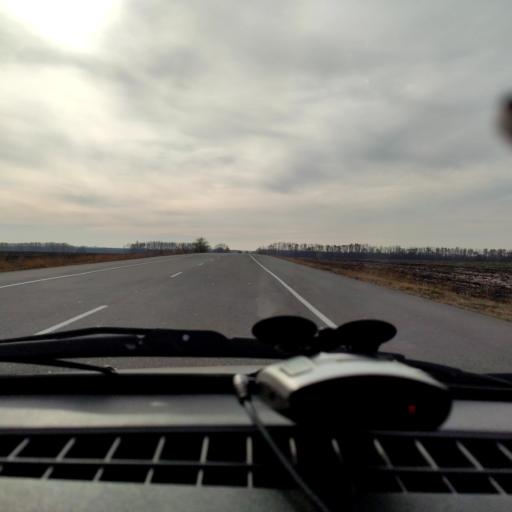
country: RU
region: Voronezj
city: Strelitsa
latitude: 51.5053
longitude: 38.9659
